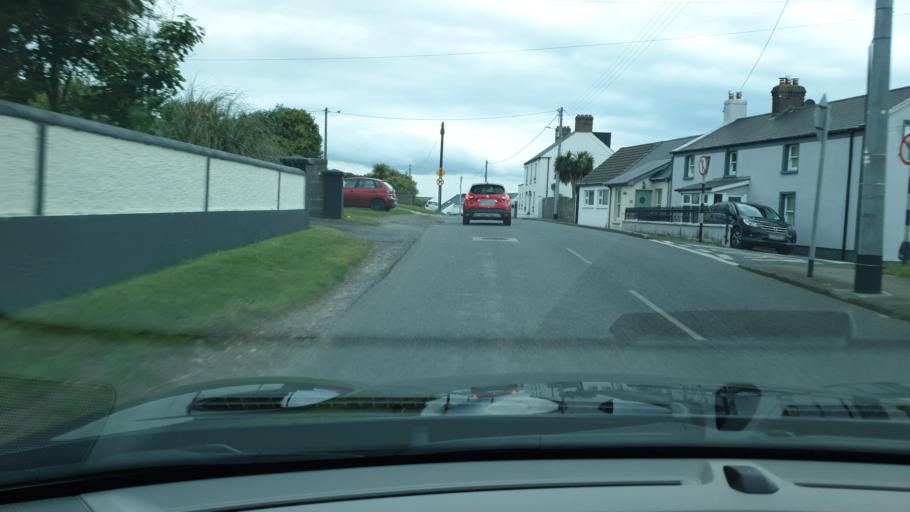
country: IE
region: Leinster
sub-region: Fingal County
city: Skerries
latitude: 53.5813
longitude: -6.1163
